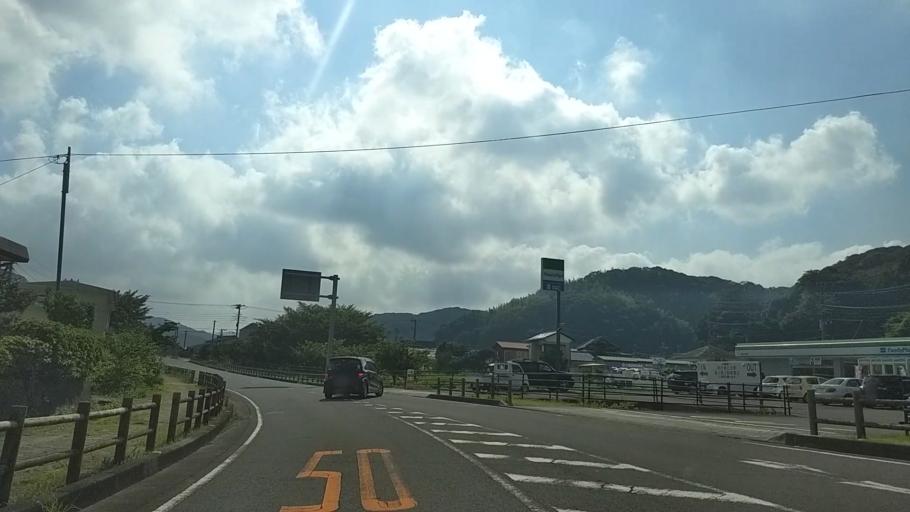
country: JP
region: Shizuoka
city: Shimoda
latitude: 34.6510
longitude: 138.8655
